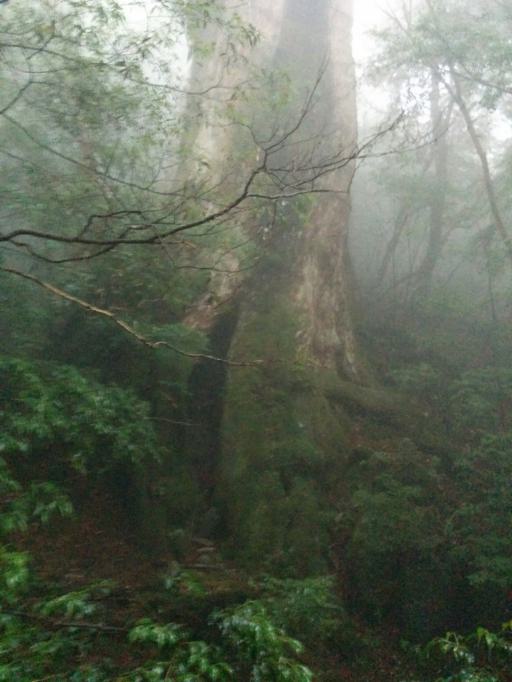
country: JP
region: Kagoshima
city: Nishinoomote
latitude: 30.3597
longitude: 130.5363
